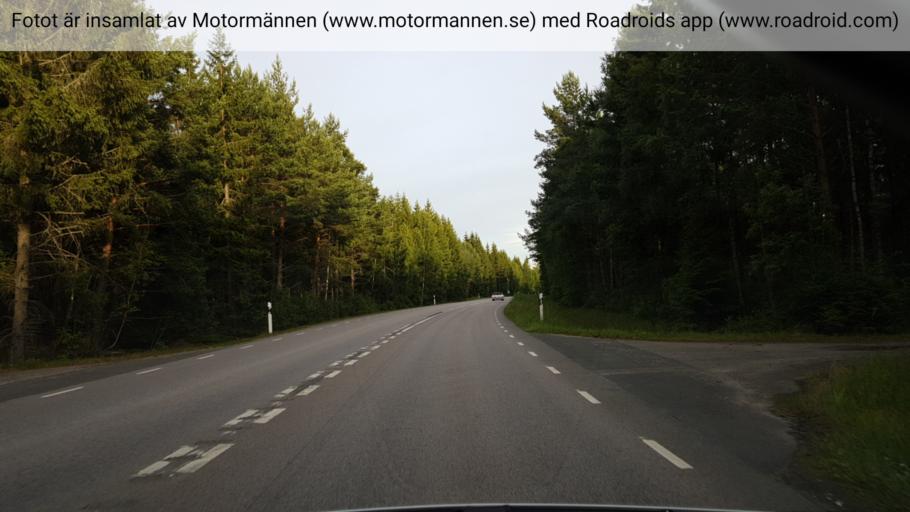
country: SE
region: Vaestra Goetaland
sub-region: Skara Kommun
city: Skara
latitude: 58.3103
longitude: 13.4611
